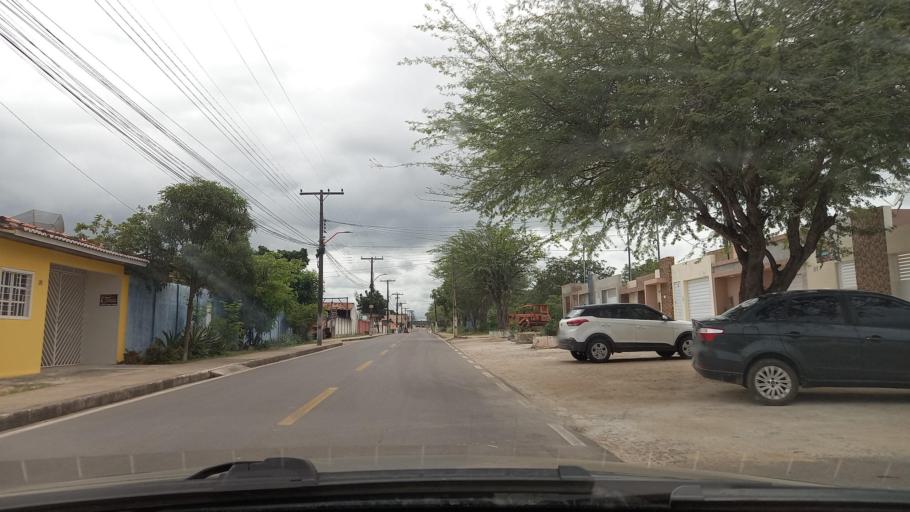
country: BR
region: Sergipe
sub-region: Caninde De Sao Francisco
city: Caninde de Sao Francisco
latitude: -9.6124
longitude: -37.7634
